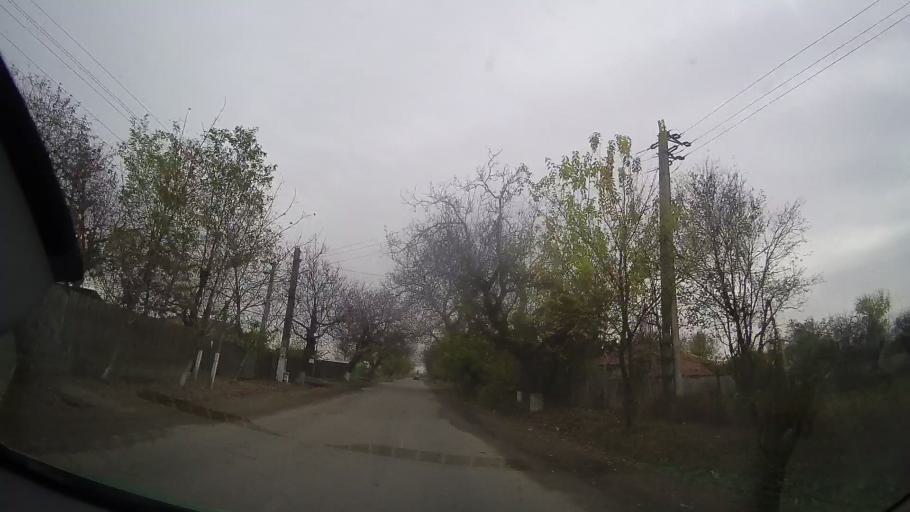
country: RO
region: Prahova
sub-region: Comuna Vadu Sapat
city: Vadu Sapat
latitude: 45.0288
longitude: 26.3909
